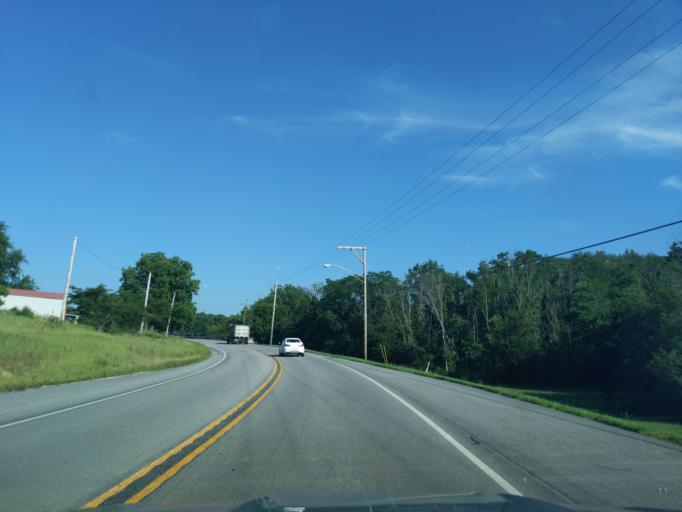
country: US
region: Indiana
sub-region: Ripley County
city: Versailles
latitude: 39.0718
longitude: -85.2688
